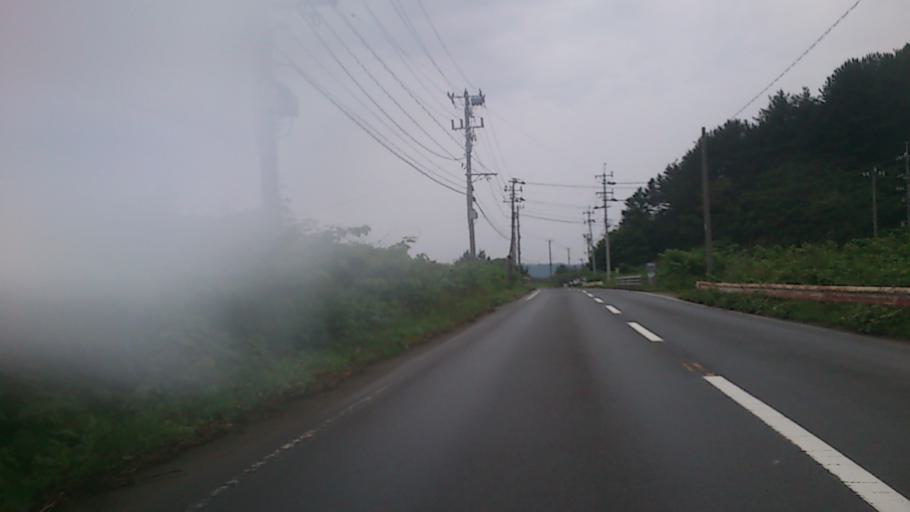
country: JP
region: Akita
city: Noshiromachi
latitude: 40.5292
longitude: 139.9487
